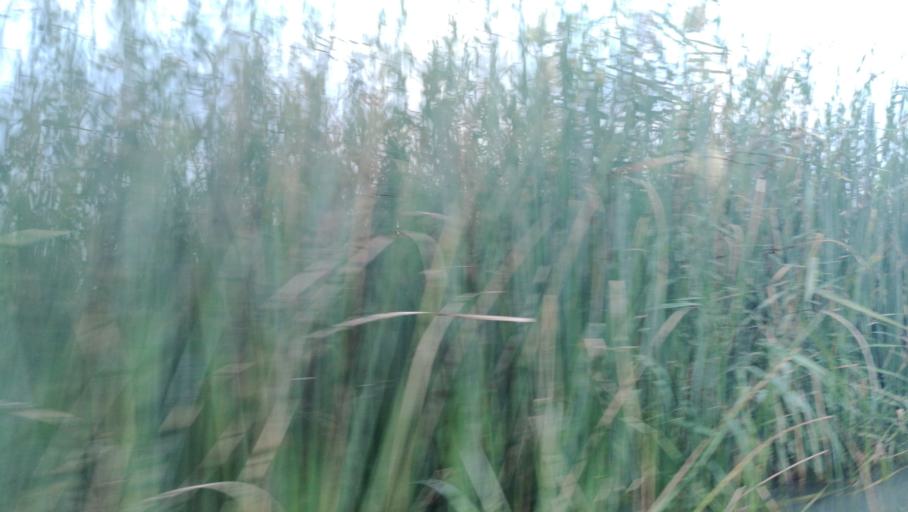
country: IQ
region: Dhi Qar
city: Al Jabayish
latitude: 30.9848
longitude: 47.0436
